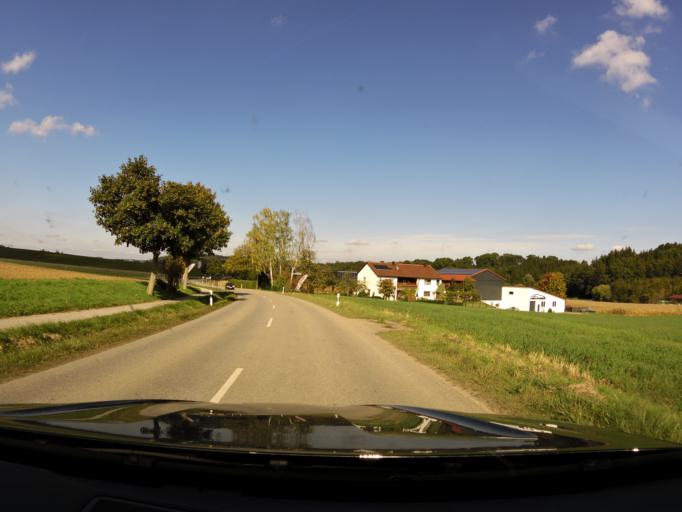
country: DE
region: Bavaria
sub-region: Lower Bavaria
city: Tiefenbach
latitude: 48.4904
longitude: 12.1008
